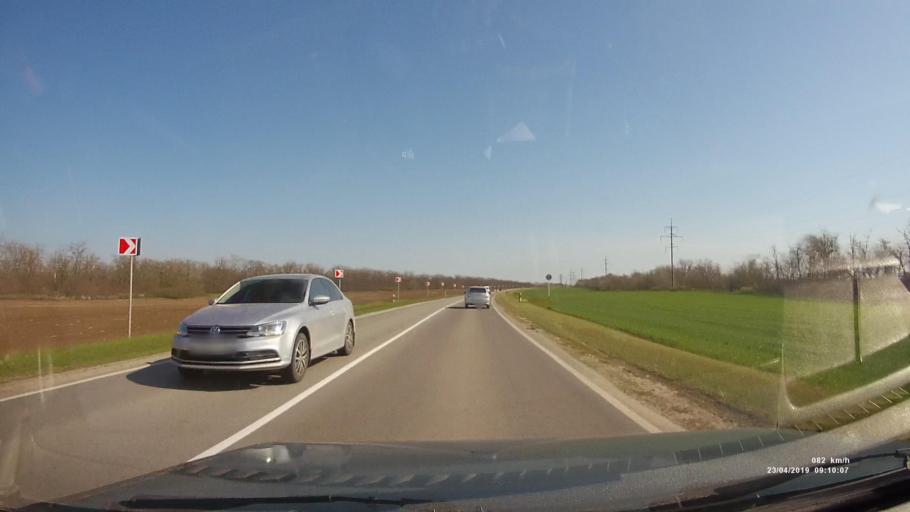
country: RU
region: Rostov
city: Sal'sk
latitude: 46.5826
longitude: 41.6178
